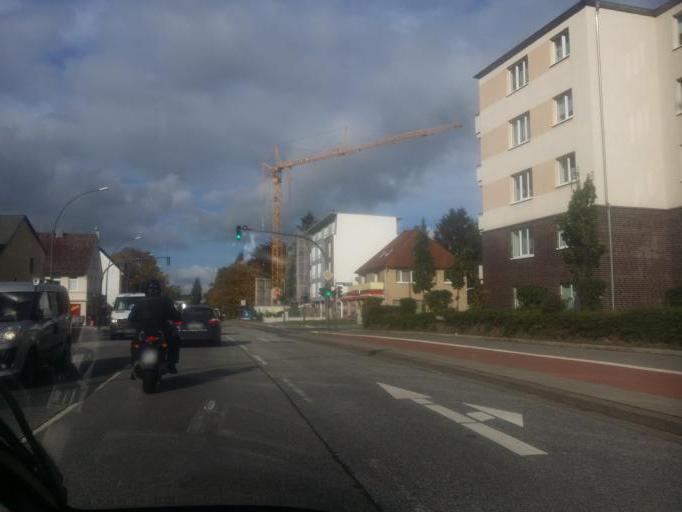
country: DE
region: Hamburg
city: Eidelstedt
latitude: 53.5931
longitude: 9.8707
